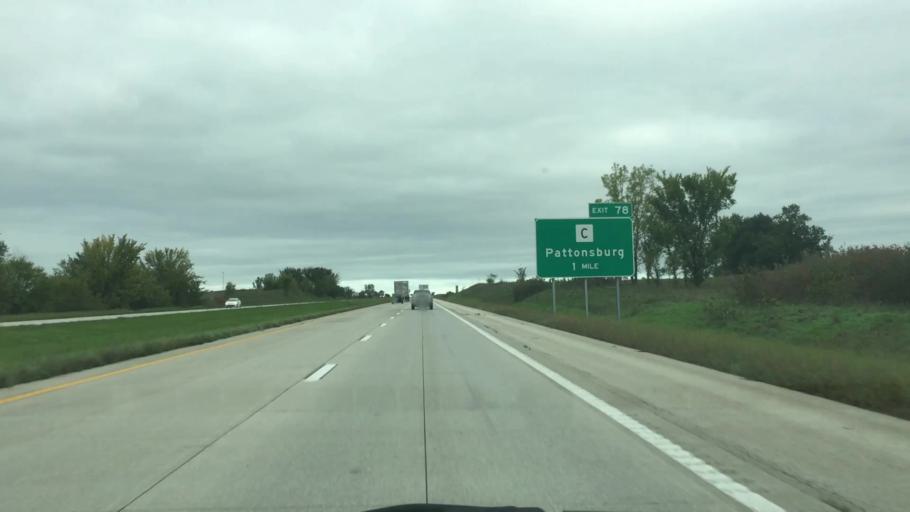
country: US
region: Missouri
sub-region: Daviess County
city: Gallatin
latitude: 40.0603
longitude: -94.0939
